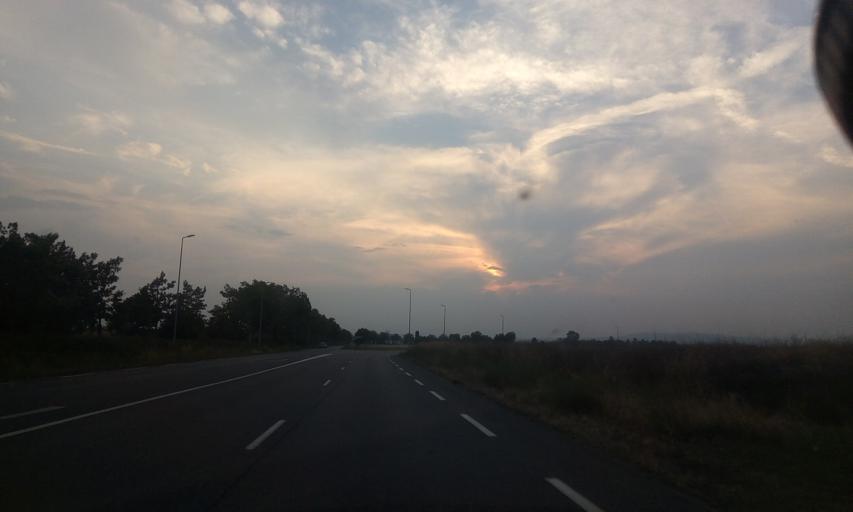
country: FR
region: Rhone-Alpes
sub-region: Departement du Rhone
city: Chassieu
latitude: 45.7419
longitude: 4.9445
